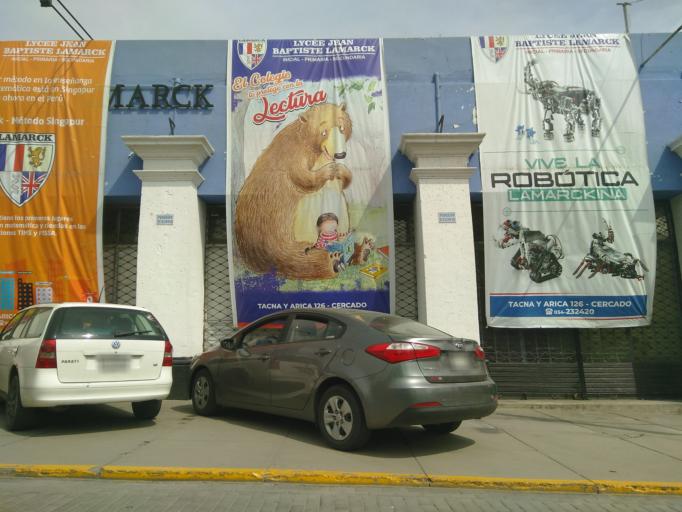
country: PE
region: Arequipa
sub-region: Provincia de Arequipa
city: Arequipa
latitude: -16.4077
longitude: -71.5402
